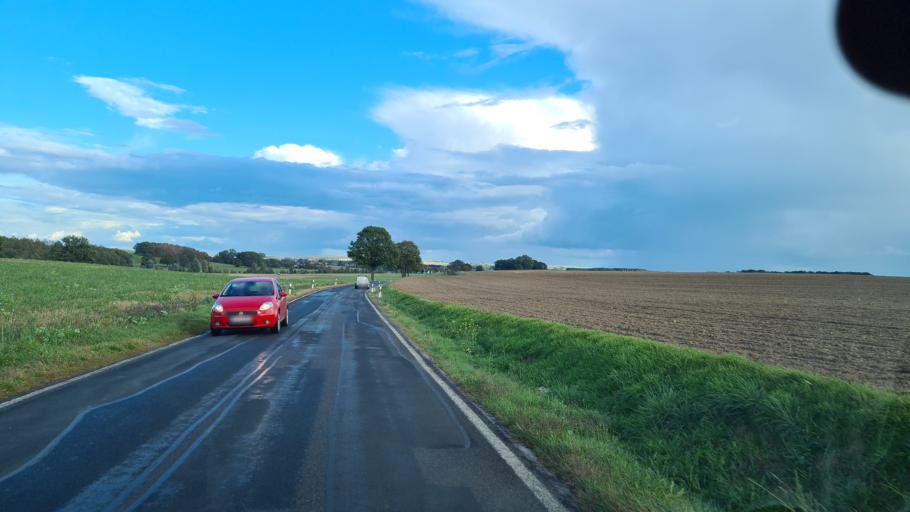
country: DE
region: Saxony
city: Dahlen
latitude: 51.3637
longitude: 13.0180
